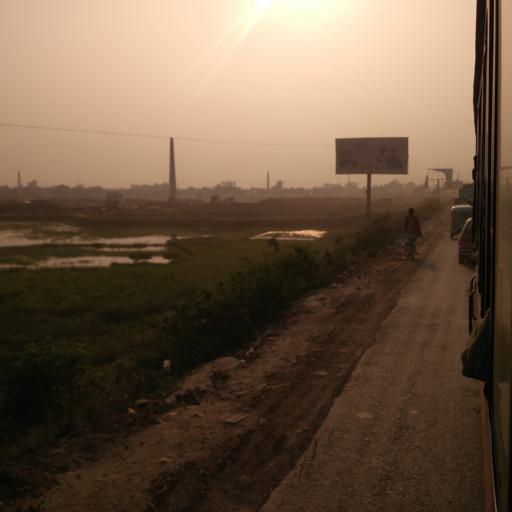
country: BD
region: Dhaka
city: Tungi
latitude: 23.8958
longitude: 90.3409
